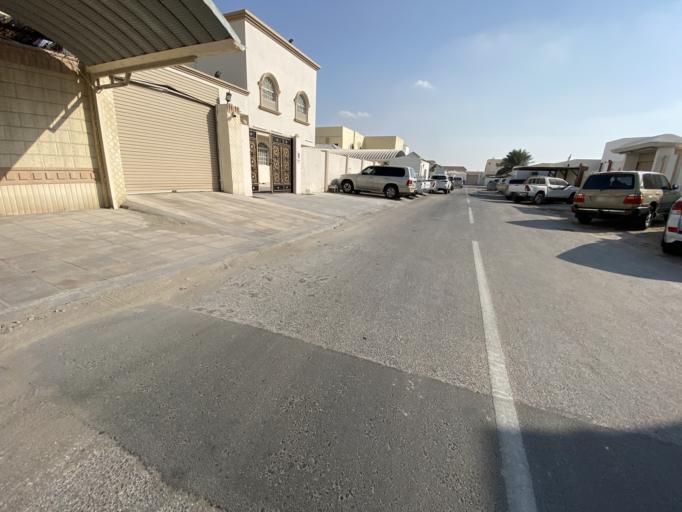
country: QA
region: Baladiyat ar Rayyan
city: Ar Rayyan
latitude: 25.2325
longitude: 51.3783
